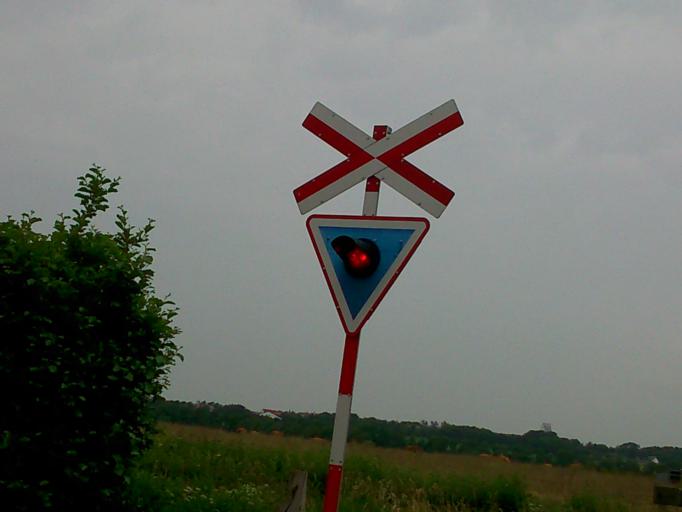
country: DK
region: Central Jutland
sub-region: Ringkobing-Skjern Kommune
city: Skjern
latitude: 55.9937
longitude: 8.4105
